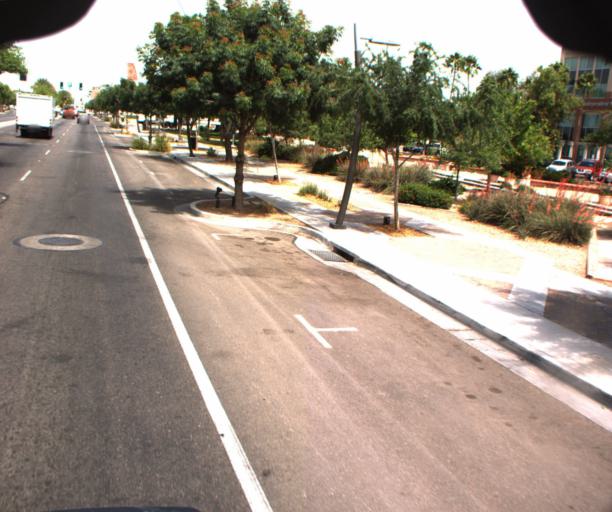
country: US
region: Arizona
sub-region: Maricopa County
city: Chandler
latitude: 33.3036
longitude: -111.8414
